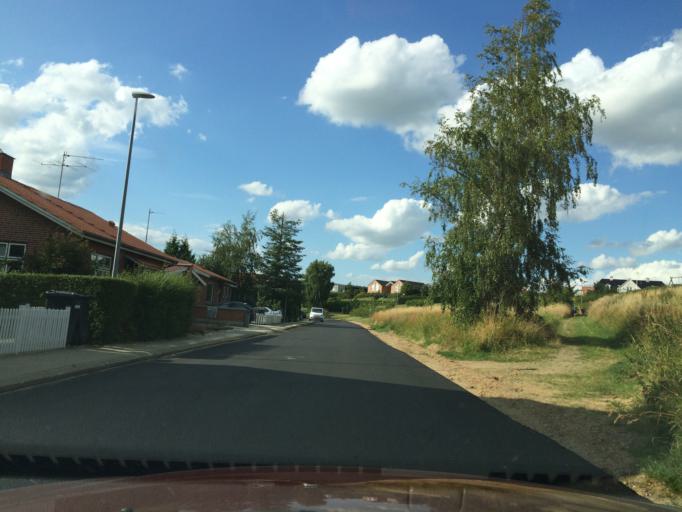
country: DK
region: Central Jutland
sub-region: Favrskov Kommune
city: Hammel
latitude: 56.2334
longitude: 9.7420
